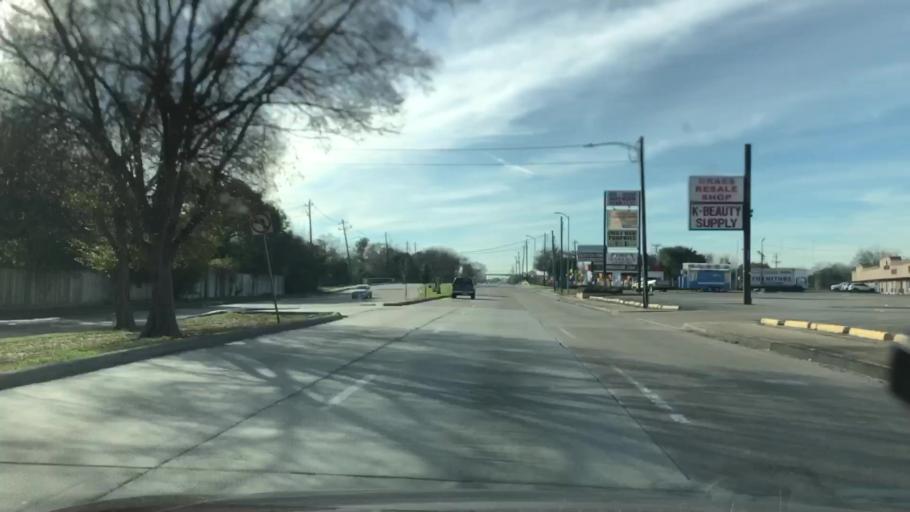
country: US
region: Texas
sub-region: Harris County
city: Bellaire
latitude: 29.6622
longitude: -95.4642
